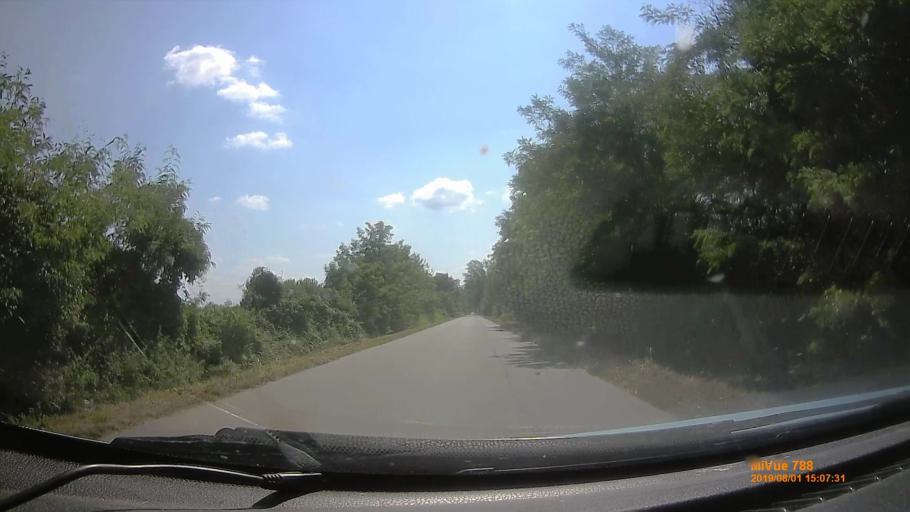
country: HU
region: Baranya
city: Sellye
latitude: 45.8582
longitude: 17.8287
